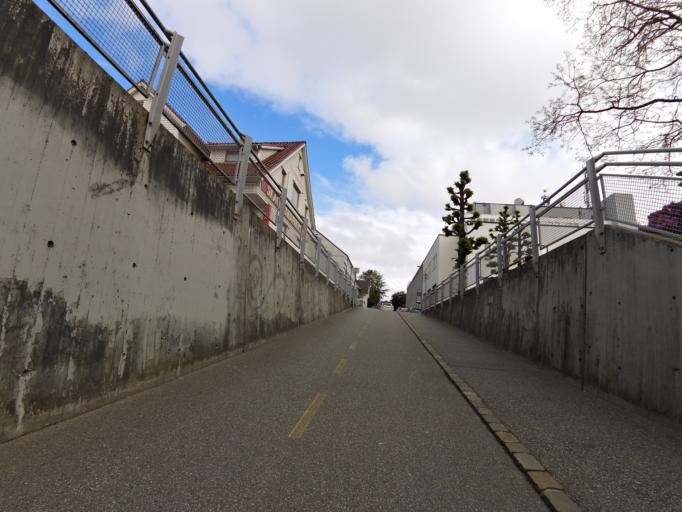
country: NO
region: Rogaland
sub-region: Stavanger
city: Stavanger
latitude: 58.9645
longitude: 5.7282
